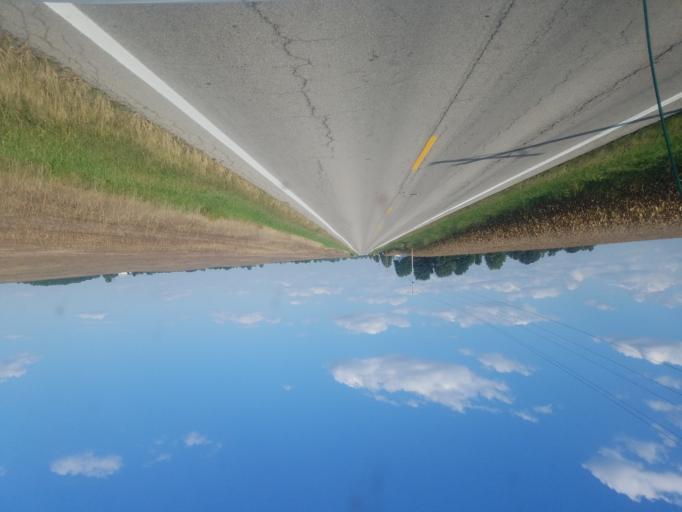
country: US
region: Ohio
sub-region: Logan County
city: Northwood
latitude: 40.4646
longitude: -83.5812
